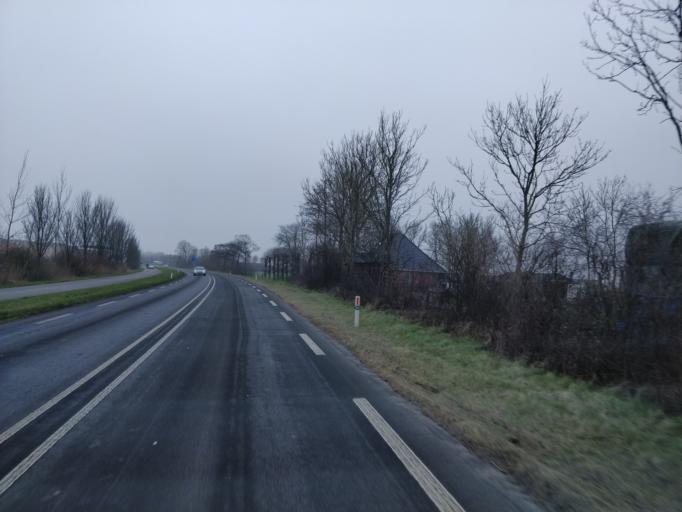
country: NL
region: Friesland
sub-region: Menameradiel
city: Berltsum
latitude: 53.2393
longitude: 5.6753
